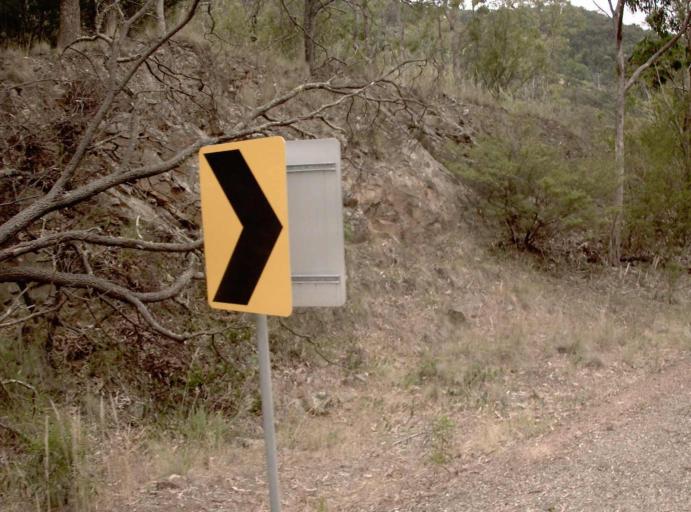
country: AU
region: Victoria
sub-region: East Gippsland
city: Bairnsdale
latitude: -37.5339
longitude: 147.2142
